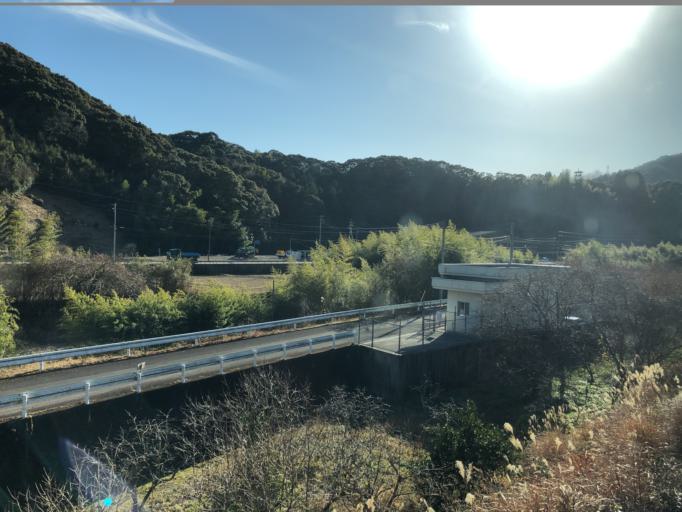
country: JP
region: Kochi
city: Nakamura
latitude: 33.1103
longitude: 133.1035
